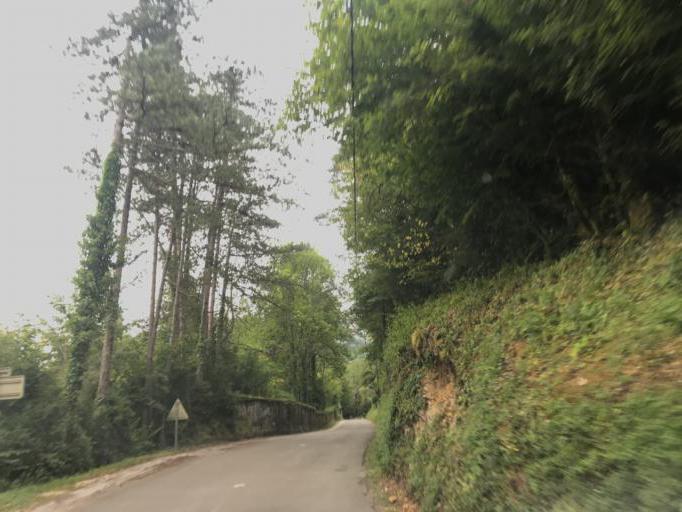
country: FR
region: Rhone-Alpes
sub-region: Departement de l'Ain
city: Dortan
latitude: 46.3463
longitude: 5.6405
